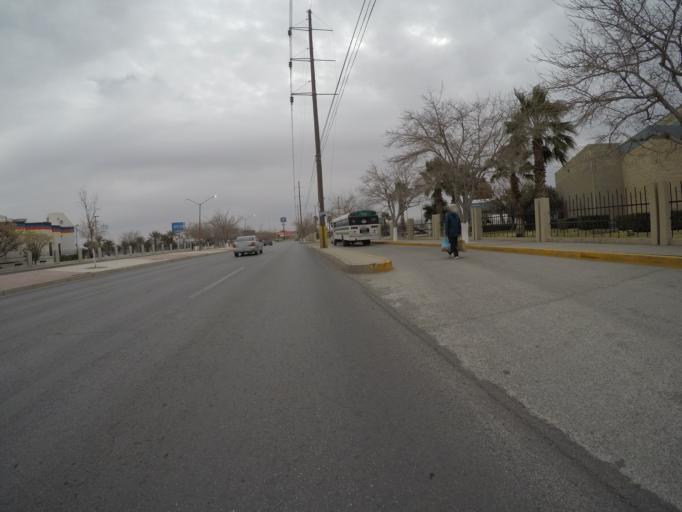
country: MX
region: Chihuahua
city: Ciudad Juarez
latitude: 31.7346
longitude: -106.4161
